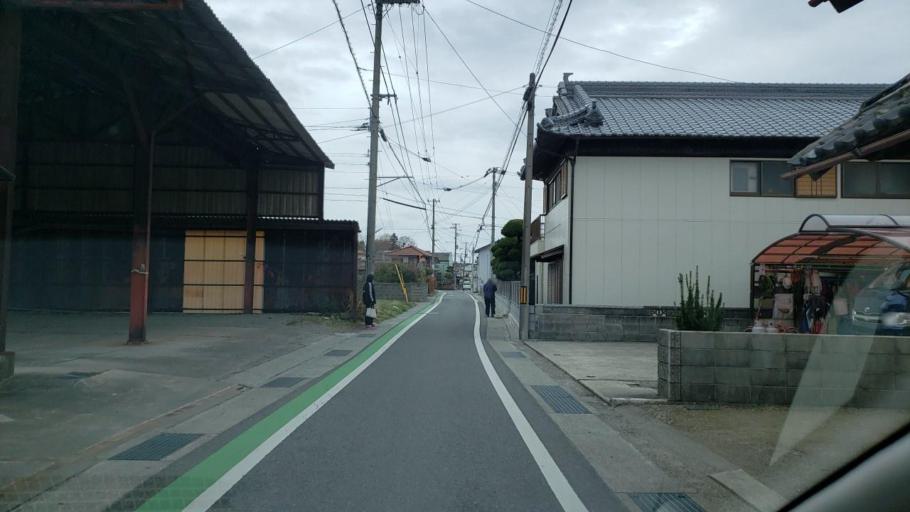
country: JP
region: Tokushima
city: Kamojimacho-jogejima
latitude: 34.0858
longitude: 134.2851
